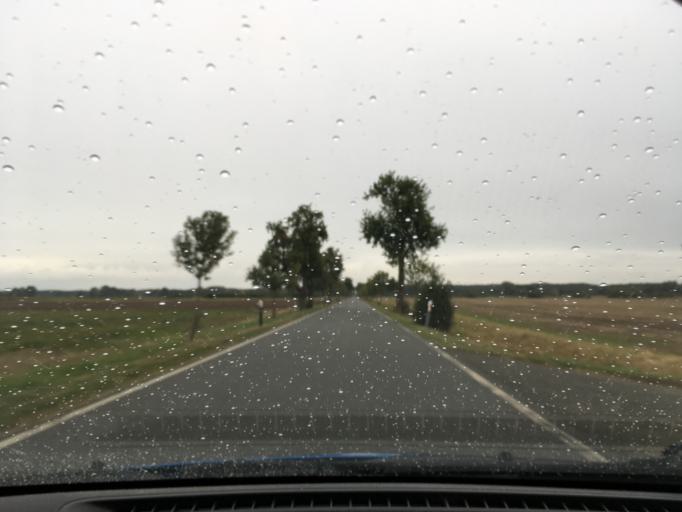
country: DE
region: Lower Saxony
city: Hitzacker
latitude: 53.2146
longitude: 10.9855
